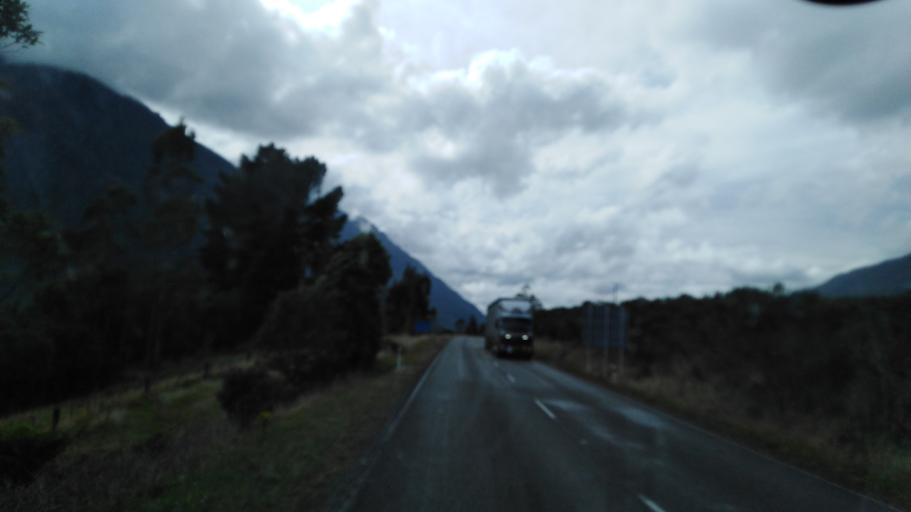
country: NZ
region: West Coast
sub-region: Grey District
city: Greymouth
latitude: -42.7436
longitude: 171.5197
